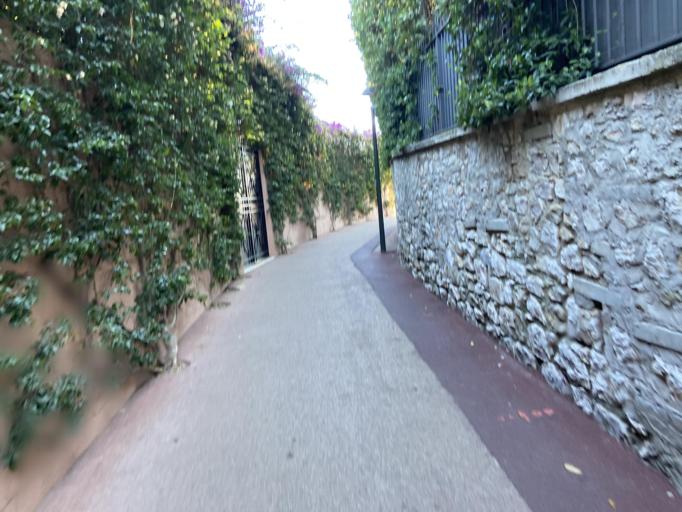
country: FR
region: Provence-Alpes-Cote d'Azur
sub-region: Departement des Alpes-Maritimes
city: Saint-Jean-Cap-Ferrat
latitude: 43.6965
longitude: 7.3324
